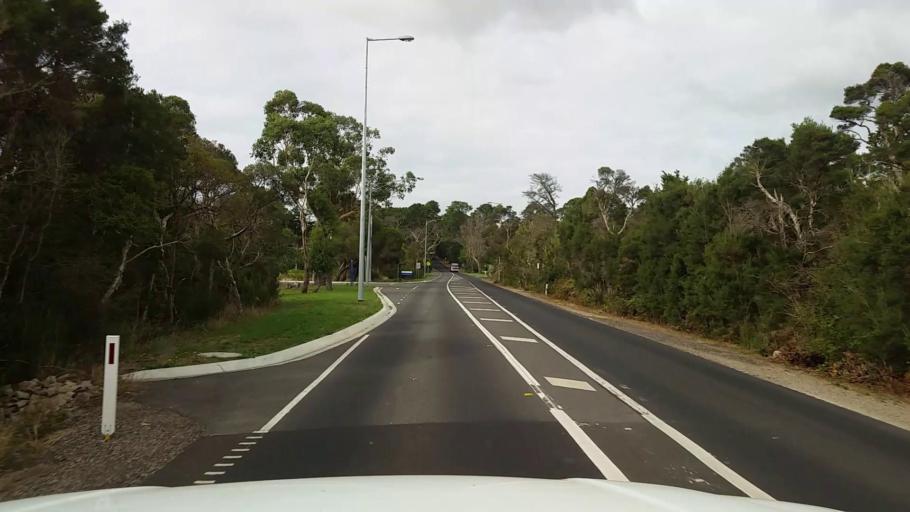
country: AU
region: Victoria
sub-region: Mornington Peninsula
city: Balnarring
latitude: -38.3623
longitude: 145.1154
